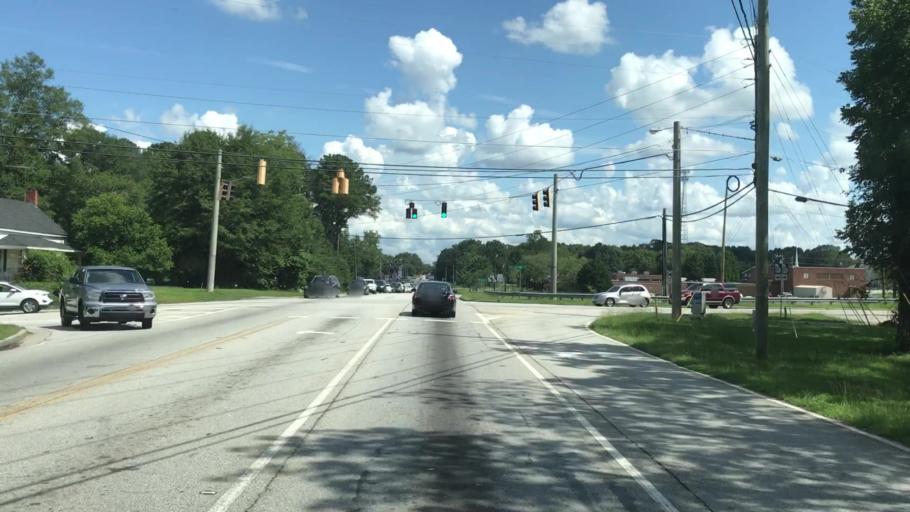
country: US
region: Georgia
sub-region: Walton County
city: Loganville
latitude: 33.8444
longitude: -83.8987
